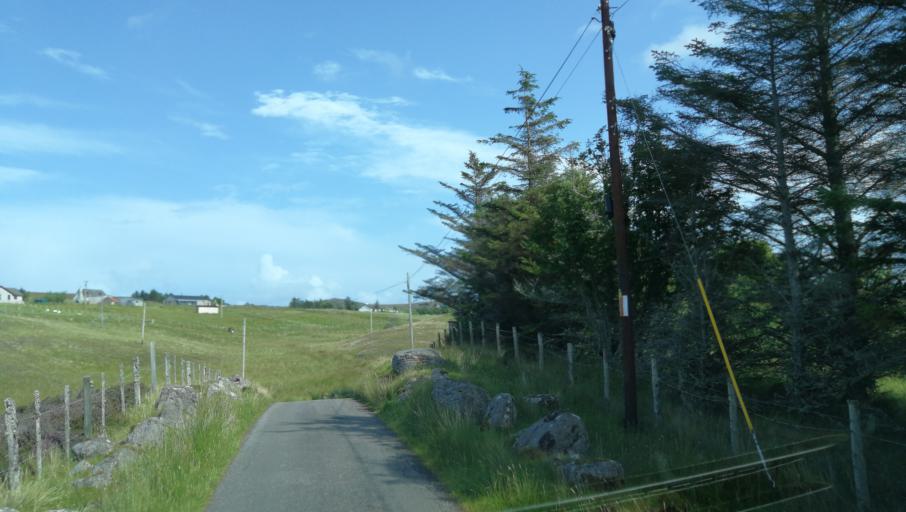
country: GB
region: Scotland
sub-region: Highland
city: Portree
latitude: 57.7457
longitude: -5.7745
